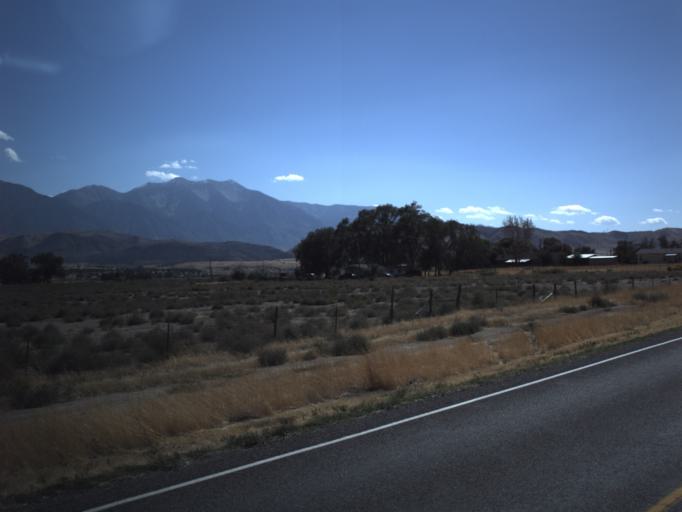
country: US
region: Utah
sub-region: Utah County
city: Genola
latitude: 39.9584
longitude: -111.9564
